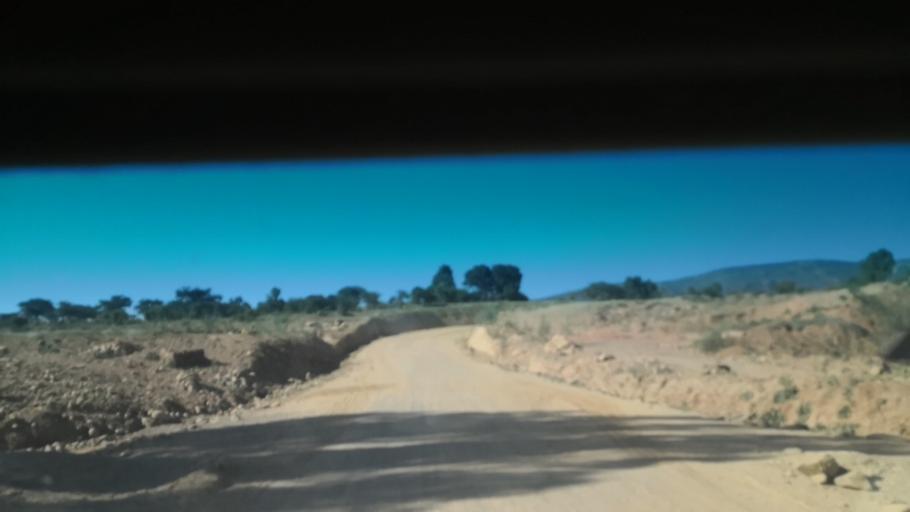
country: ET
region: Tigray
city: Mekele
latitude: 13.8467
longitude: 39.5126
